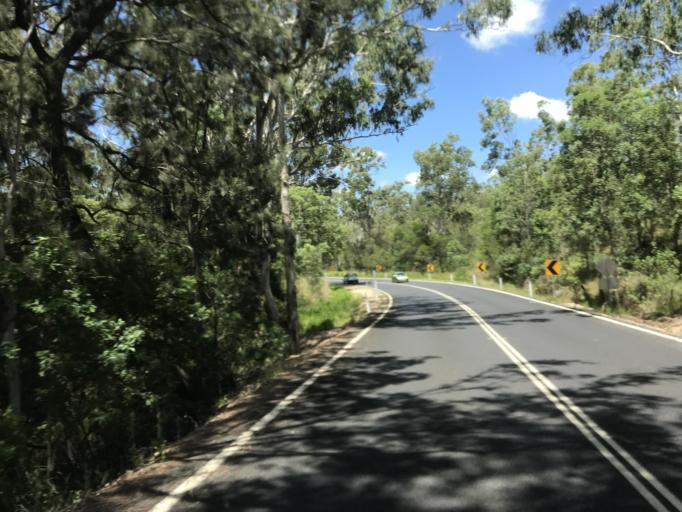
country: AU
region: Queensland
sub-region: Tablelands
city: Atherton
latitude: -17.4041
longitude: 145.3892
